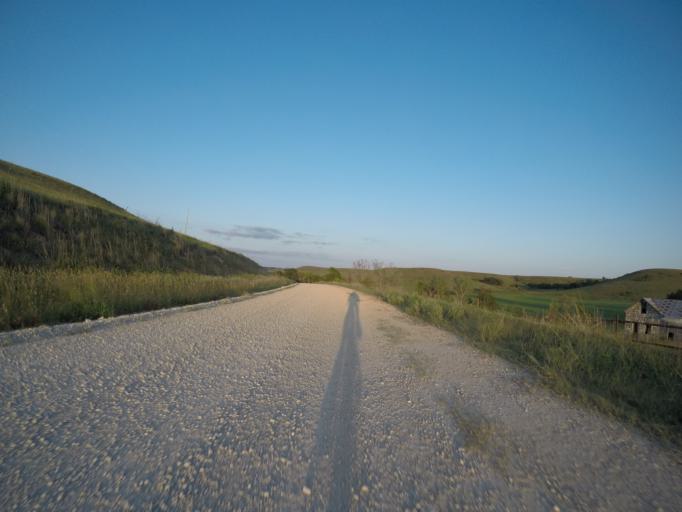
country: US
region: Kansas
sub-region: Riley County
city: Ogden
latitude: 39.0053
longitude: -96.6184
